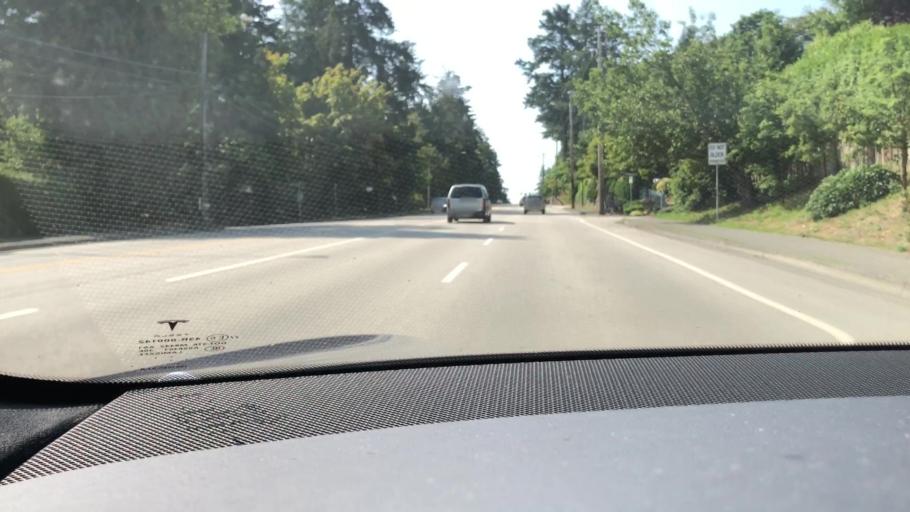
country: US
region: Washington
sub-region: Whatcom County
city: Point Roberts
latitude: 49.0077
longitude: -123.0687
